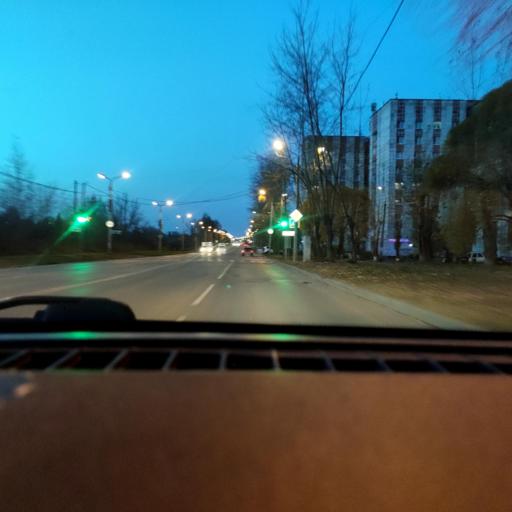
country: RU
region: Perm
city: Perm
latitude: 58.0603
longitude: 56.3602
